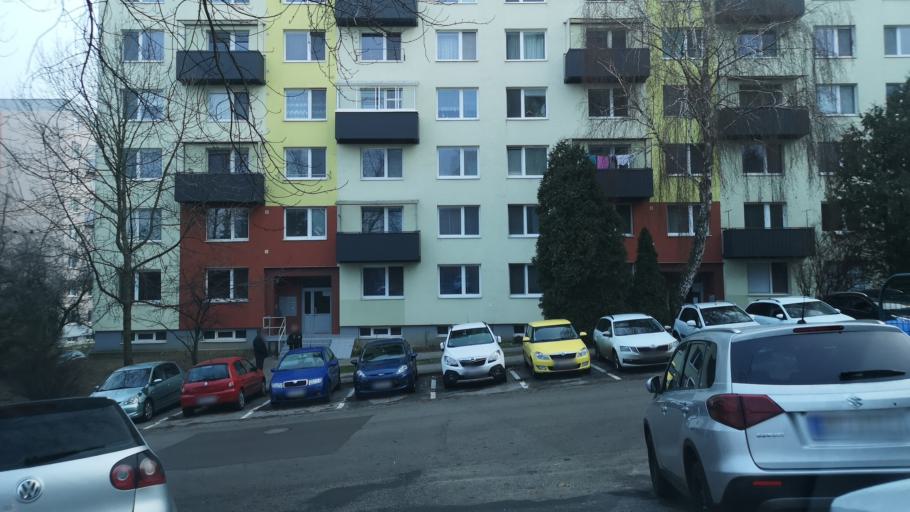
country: SK
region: Nitriansky
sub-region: Okres Nitra
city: Nitra
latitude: 48.3036
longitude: 18.0575
